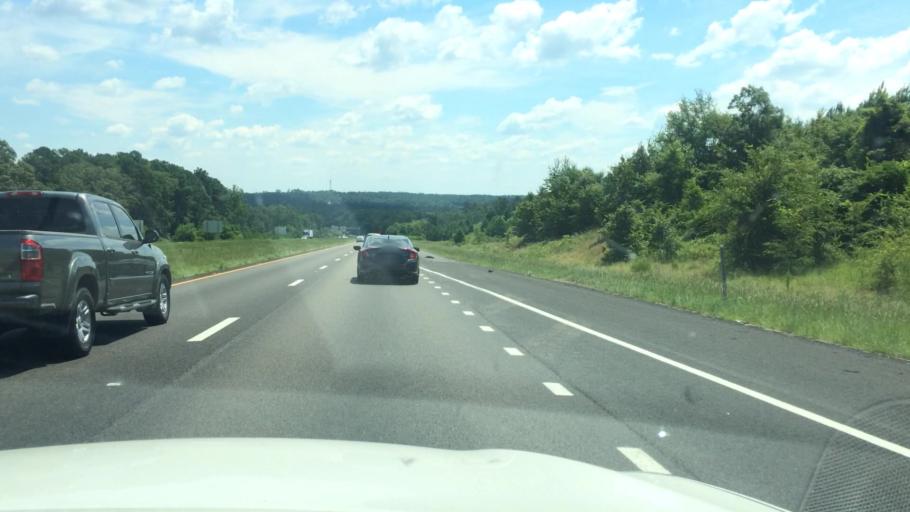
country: US
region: South Carolina
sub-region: Edgefield County
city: Murphys Estates
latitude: 33.5677
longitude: -81.9255
